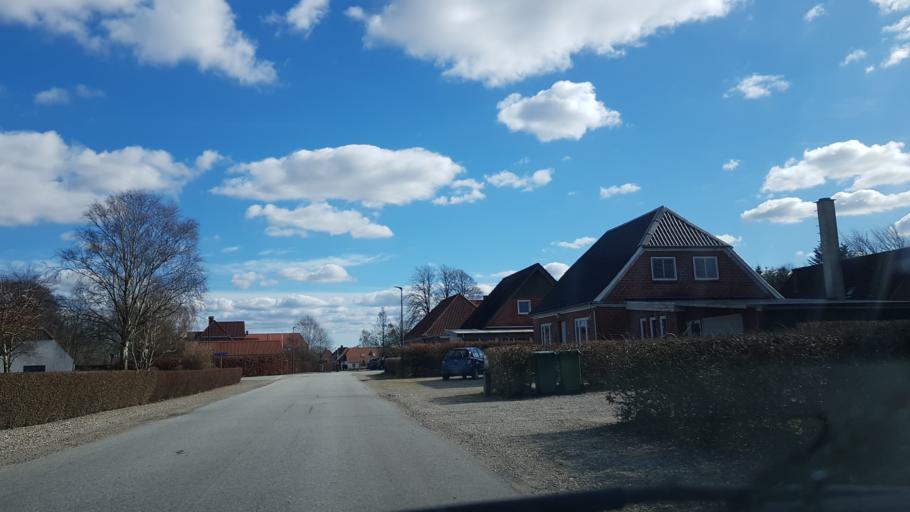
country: DK
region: South Denmark
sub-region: Vejen Kommune
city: Rodding
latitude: 55.3926
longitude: 9.0364
